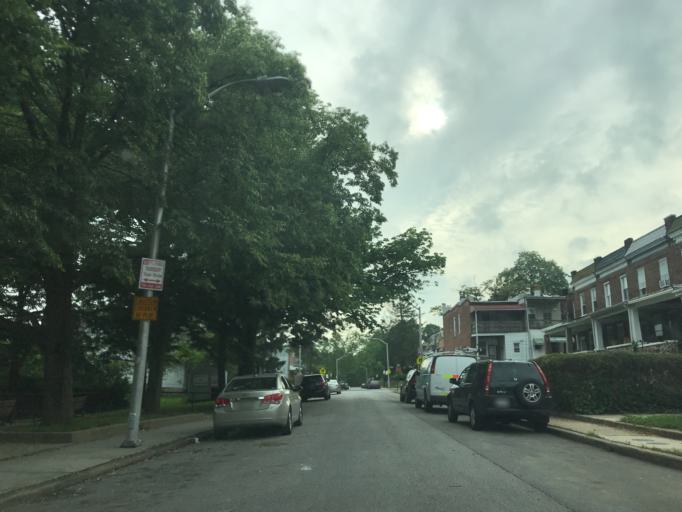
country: US
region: Maryland
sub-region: Baltimore County
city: Charlestown
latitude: 39.3044
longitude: -76.6694
